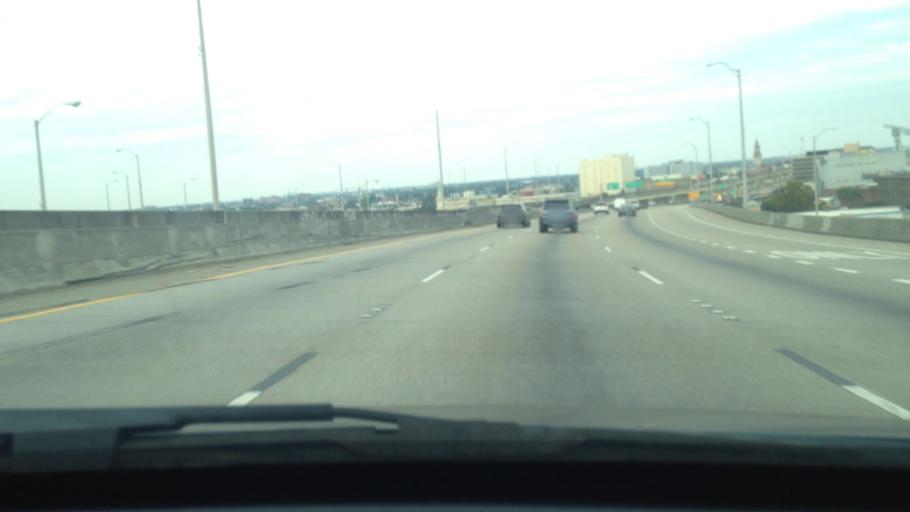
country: US
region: Louisiana
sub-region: Orleans Parish
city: New Orleans
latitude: 29.9388
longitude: -90.0653
